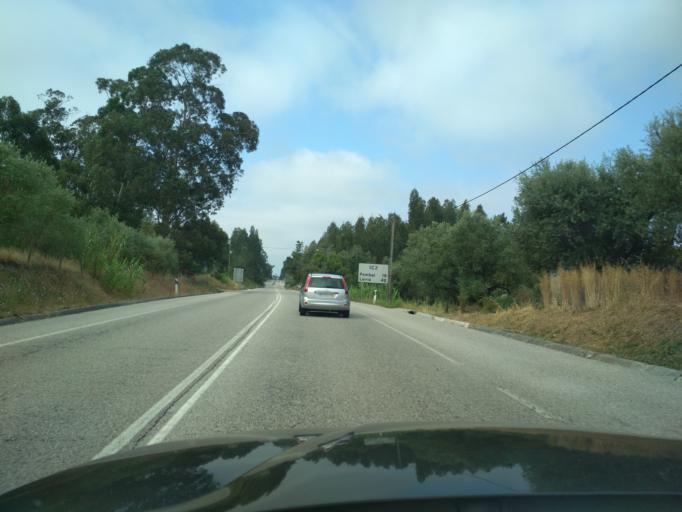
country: PT
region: Coimbra
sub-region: Soure
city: Soure
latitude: 40.0545
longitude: -8.5478
